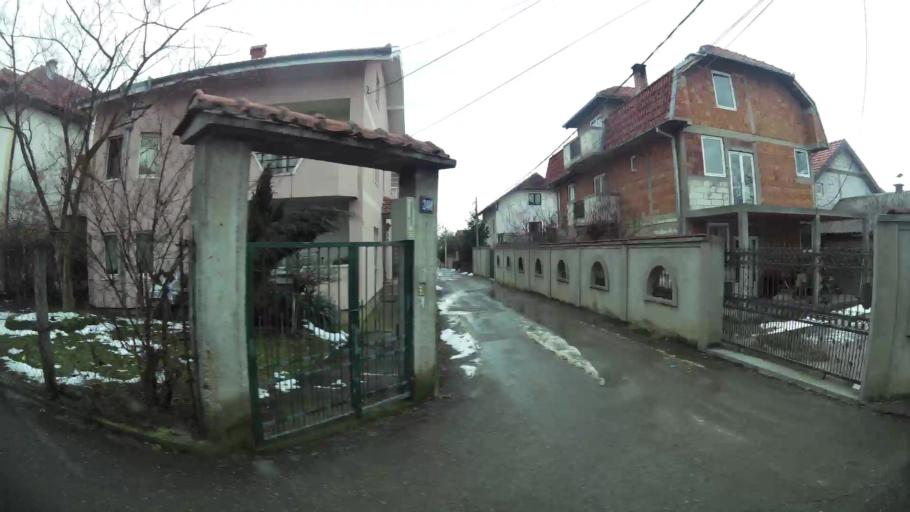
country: RS
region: Central Serbia
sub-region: Belgrade
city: Rakovica
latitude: 44.7424
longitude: 20.3954
